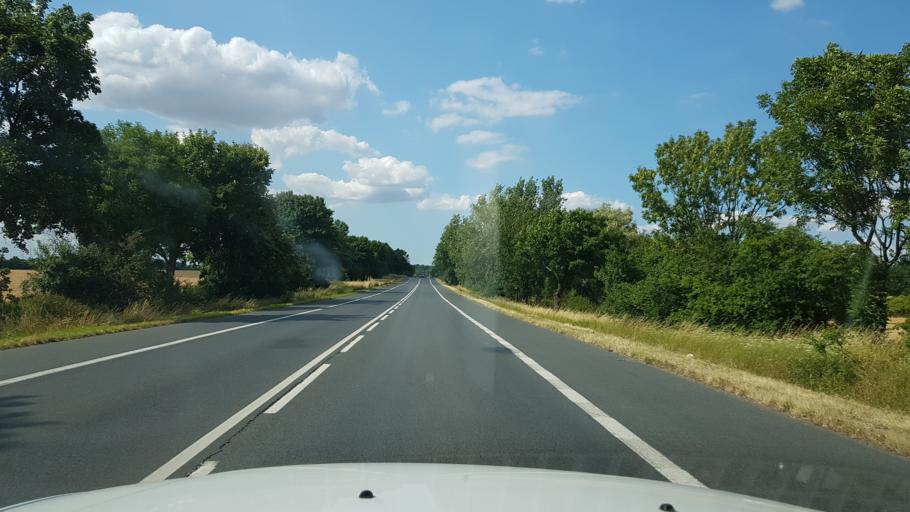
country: PL
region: West Pomeranian Voivodeship
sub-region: Powiat pyrzycki
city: Pyrzyce
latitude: 53.1172
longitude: 14.8928
